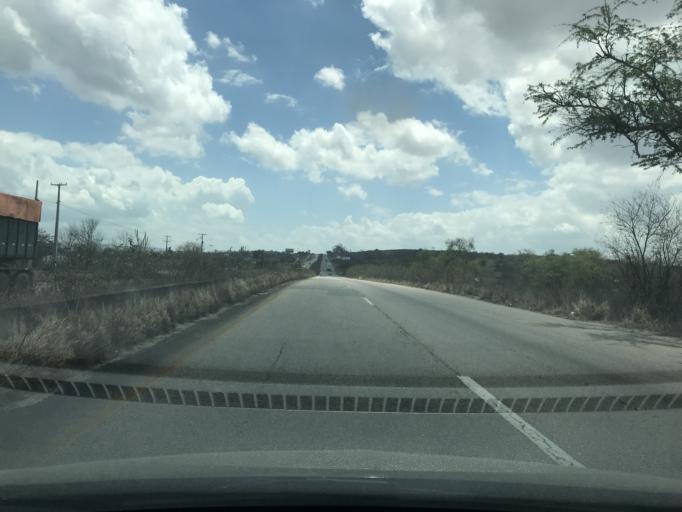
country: BR
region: Pernambuco
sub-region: Caruaru
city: Caruaru
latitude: -8.3022
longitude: -35.9190
